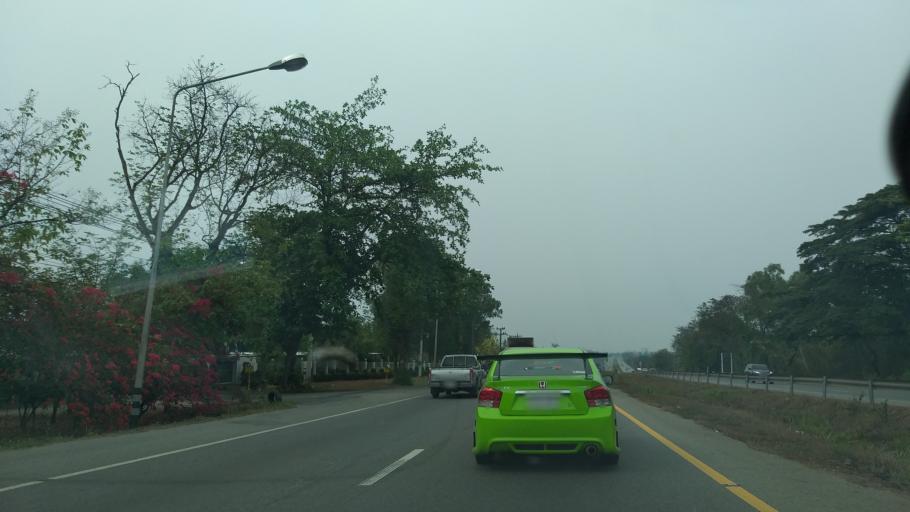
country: TH
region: Chon Buri
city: Ko Chan
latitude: 13.3313
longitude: 101.2703
